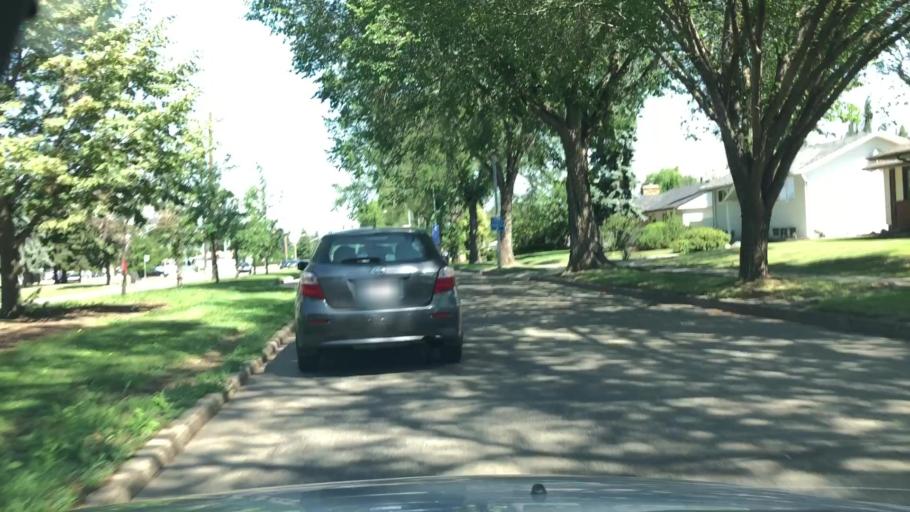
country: CA
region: Alberta
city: Edmonton
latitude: 53.5501
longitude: -113.4185
